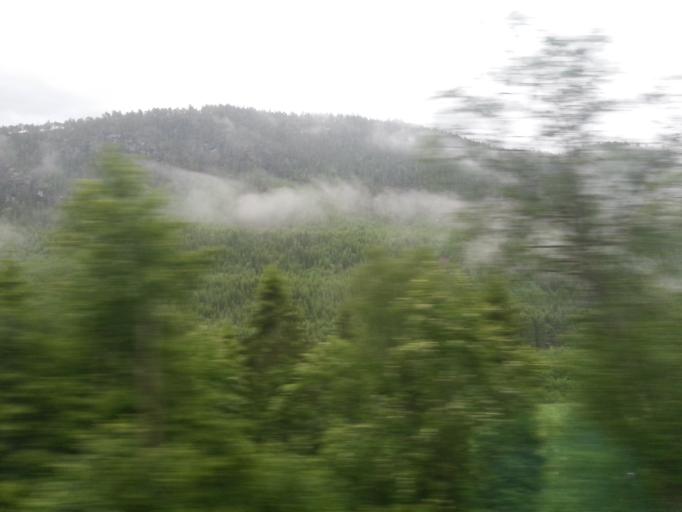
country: NO
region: Sor-Trondelag
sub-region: Midtre Gauldal
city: Storen
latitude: 63.0083
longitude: 10.2373
